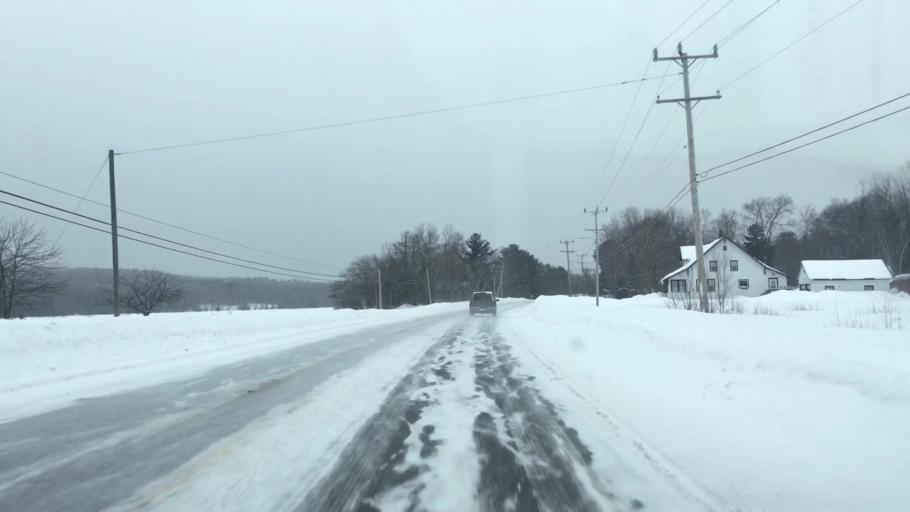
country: US
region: Maine
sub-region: Penobscot County
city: Medway
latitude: 45.5953
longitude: -68.4905
